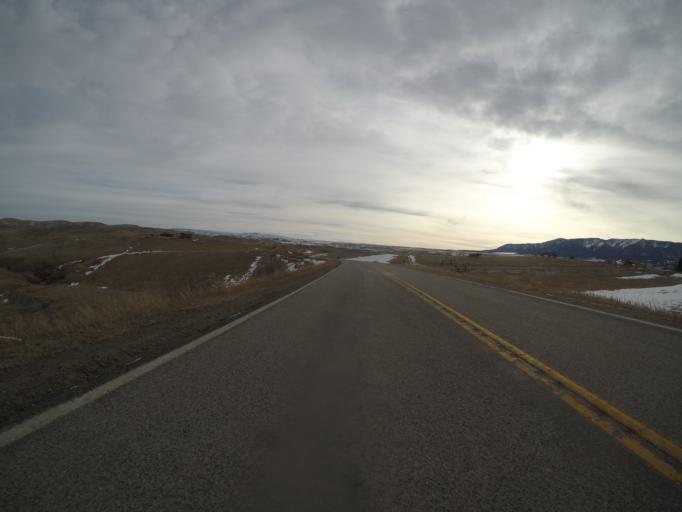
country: US
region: Montana
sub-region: Stillwater County
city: Absarokee
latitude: 45.3163
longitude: -109.4327
